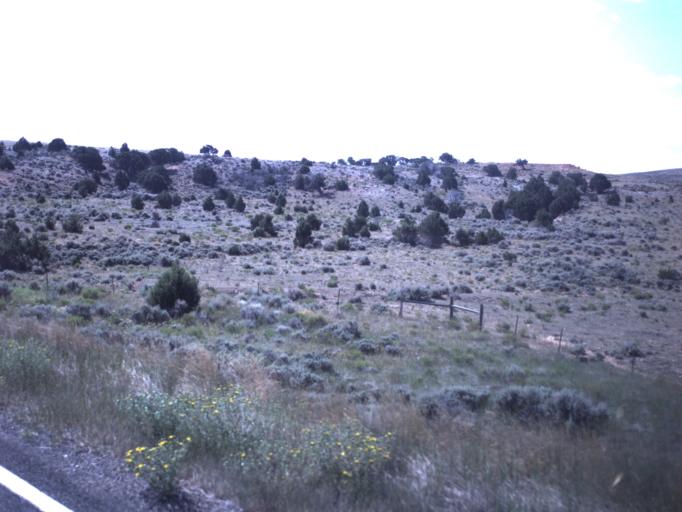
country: US
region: Utah
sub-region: Daggett County
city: Manila
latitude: 40.9831
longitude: -109.8417
